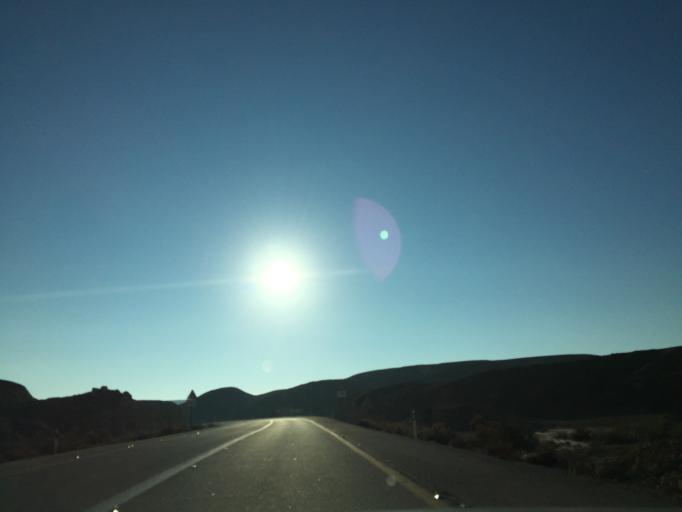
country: IL
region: Southern District
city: Mitzpe Ramon
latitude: 30.5296
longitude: 34.9243
